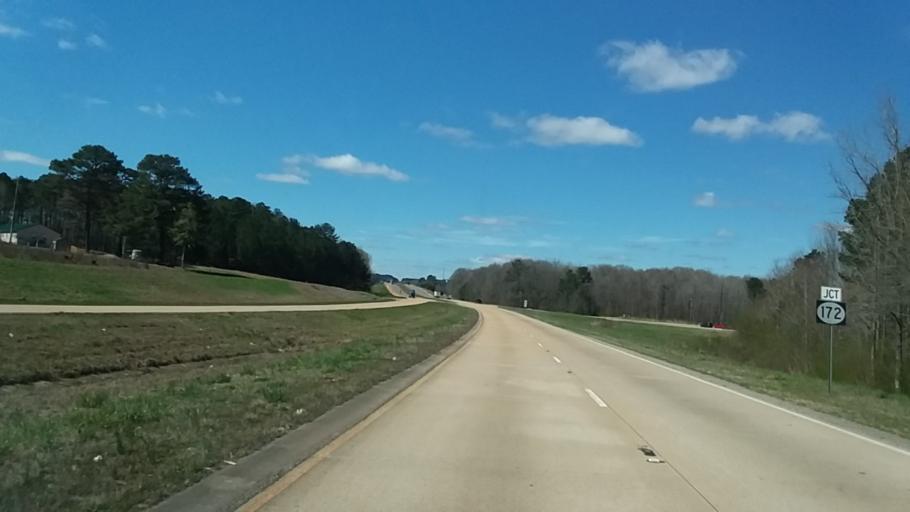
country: US
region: Mississippi
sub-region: Tishomingo County
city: Iuka
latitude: 34.8221
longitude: -88.2938
